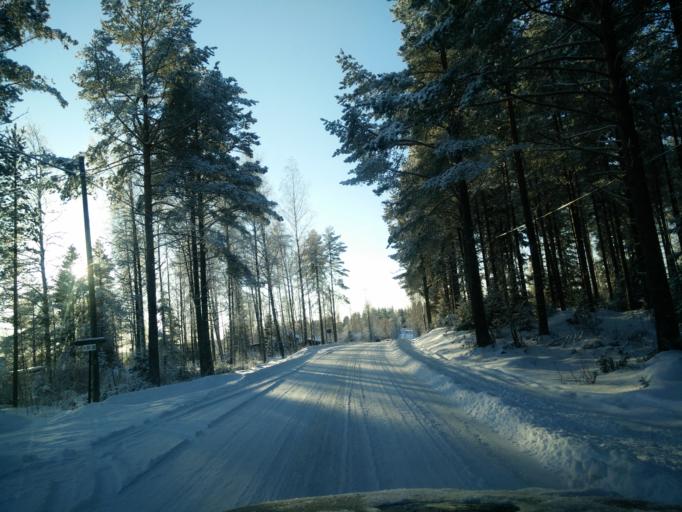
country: SE
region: Vaesternorrland
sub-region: Sundsvalls Kommun
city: Njurundabommen
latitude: 62.2308
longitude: 17.5042
